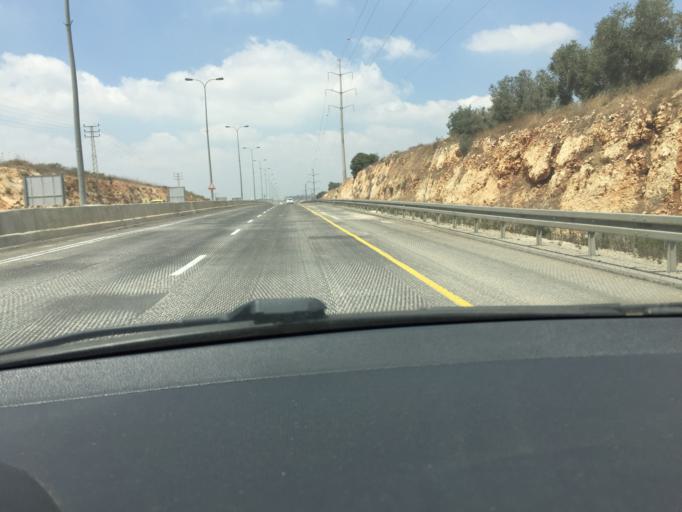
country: PS
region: West Bank
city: Kifil Haris
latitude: 32.1097
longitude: 35.1636
